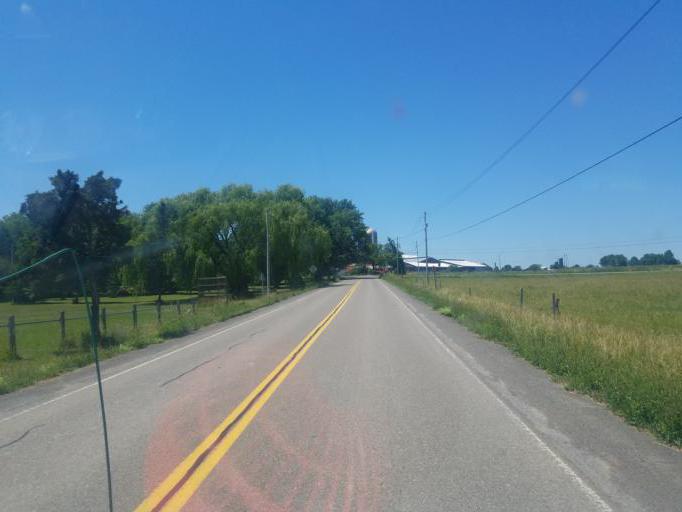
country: US
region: New York
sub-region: Yates County
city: Penn Yan
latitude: 42.6796
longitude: -77.0008
